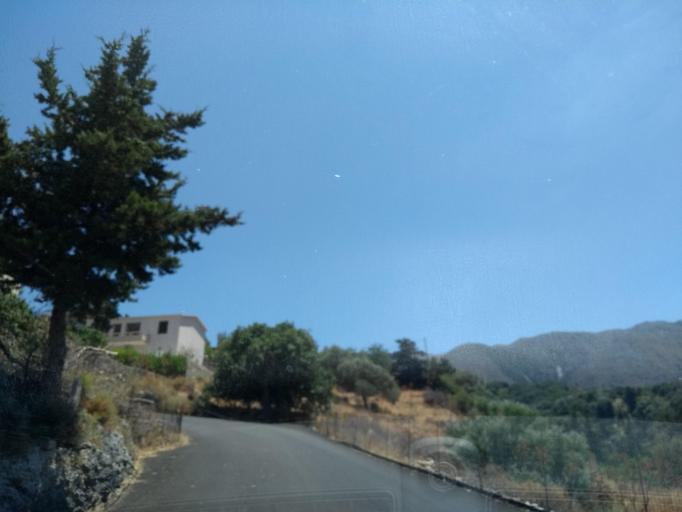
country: GR
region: Crete
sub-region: Nomos Chanias
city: Georgioupolis
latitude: 35.3156
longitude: 24.3085
